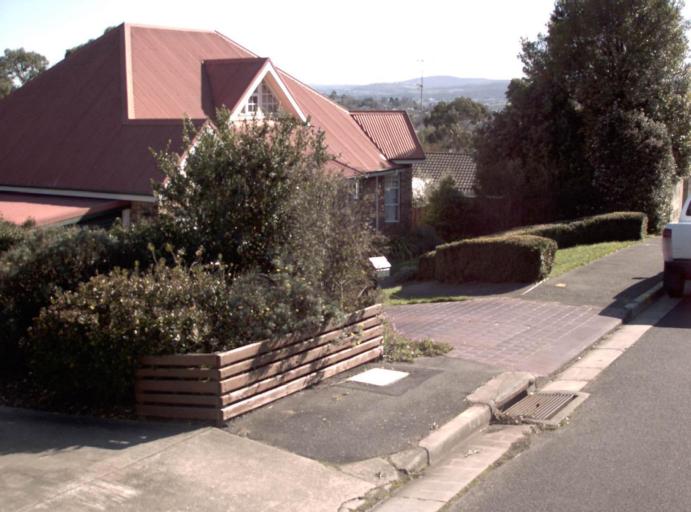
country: AU
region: Tasmania
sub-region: Launceston
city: East Launceston
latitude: -41.4533
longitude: 147.1630
